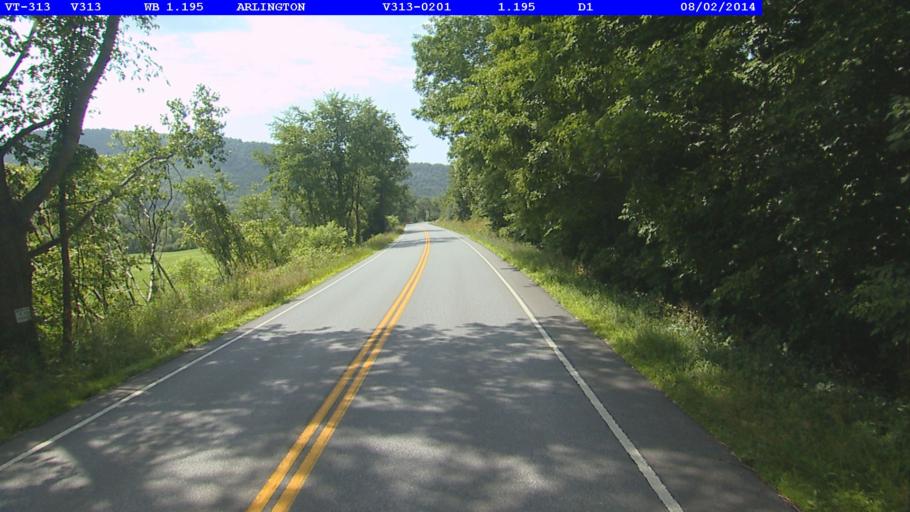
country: US
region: Vermont
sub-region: Bennington County
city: Arlington
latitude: 43.1021
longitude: -73.2431
